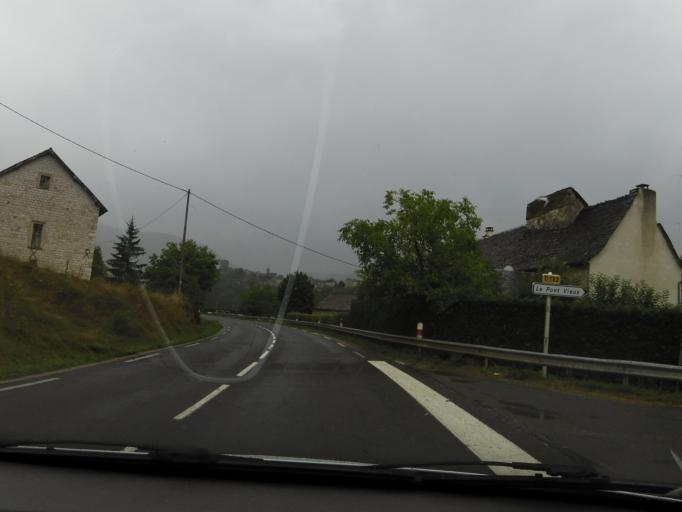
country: FR
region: Languedoc-Roussillon
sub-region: Departement de la Lozere
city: Chanac
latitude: 44.4713
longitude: 3.3354
